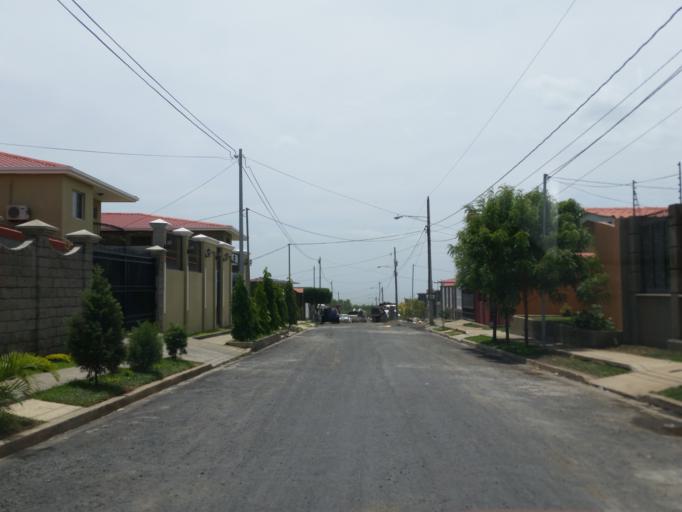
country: NI
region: Managua
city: Managua
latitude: 12.1096
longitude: -86.2423
